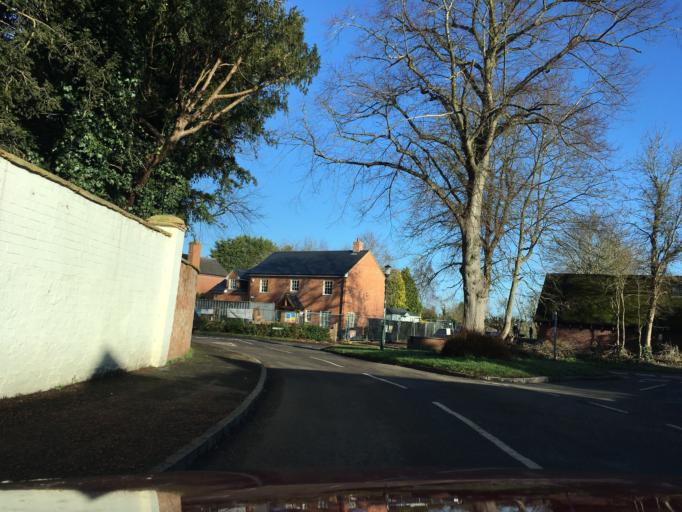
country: GB
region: England
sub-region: Warwickshire
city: Stratford-upon-Avon
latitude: 52.2071
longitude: -1.6579
